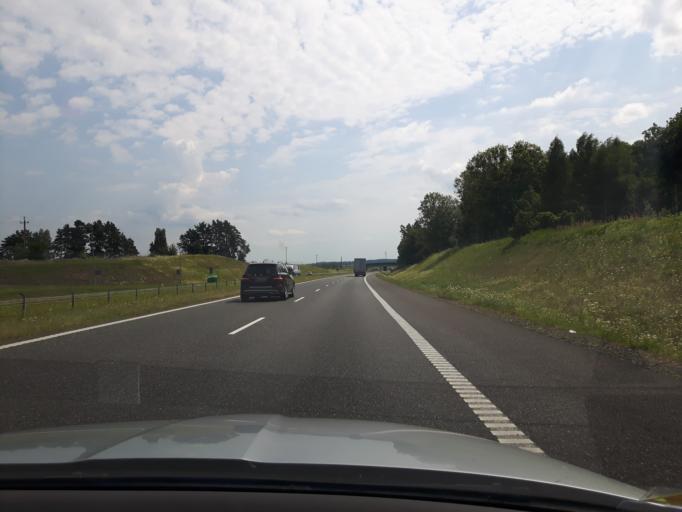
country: PL
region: Warmian-Masurian Voivodeship
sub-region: Powiat olsztynski
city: Olsztynek
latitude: 53.5143
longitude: 20.2980
